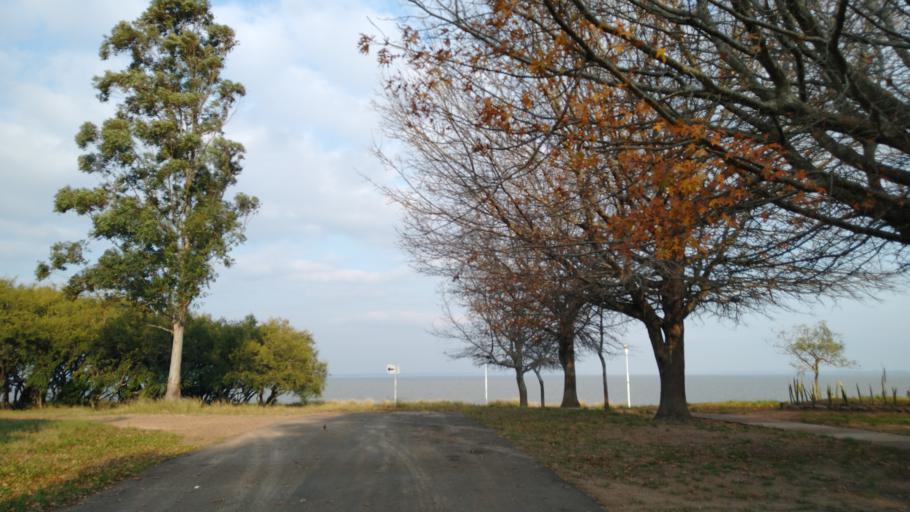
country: AR
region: Entre Rios
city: Santa Ana
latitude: -30.9144
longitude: -57.9269
